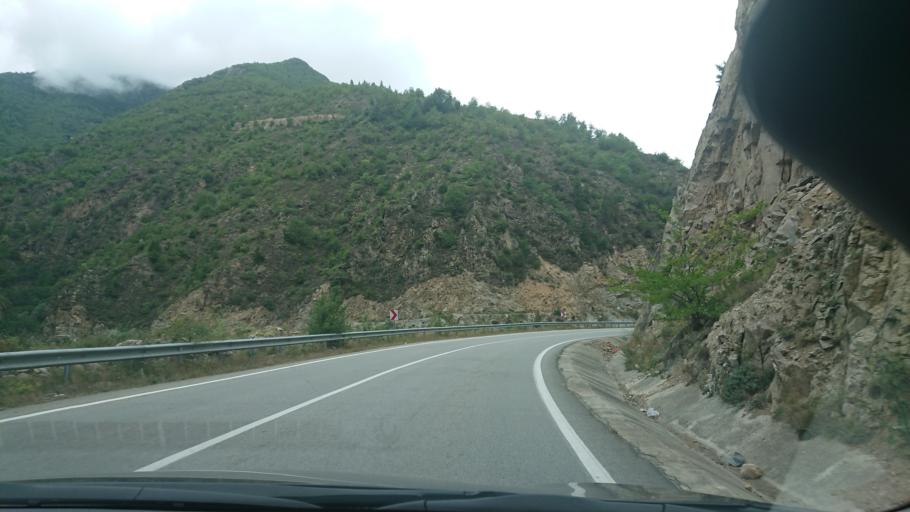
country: TR
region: Gumushane
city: Kurtun
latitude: 40.7052
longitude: 39.0669
